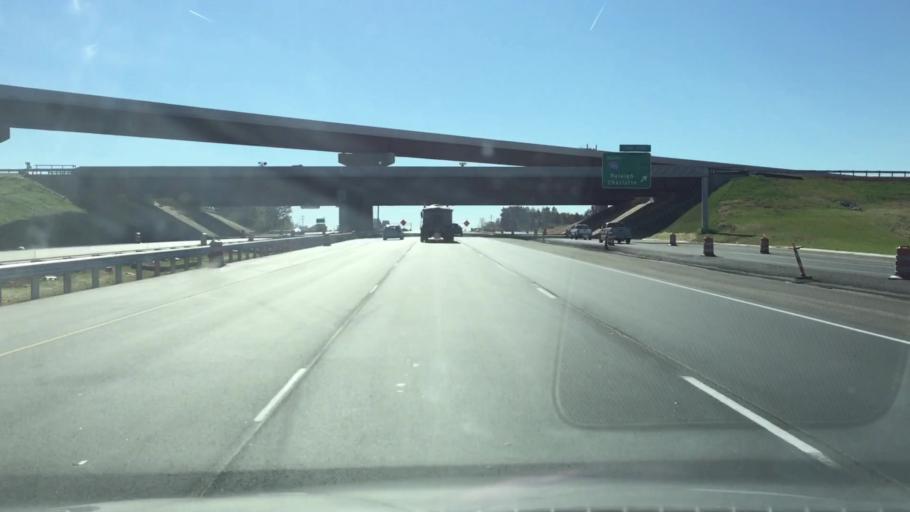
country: US
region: North Carolina
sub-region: Guilford County
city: McLeansville
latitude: 36.1442
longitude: -79.7347
